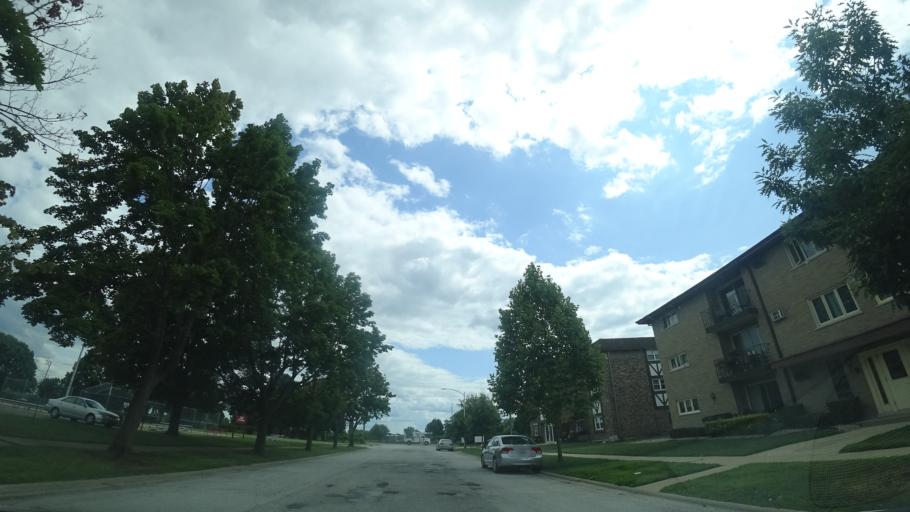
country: US
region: Illinois
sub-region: Cook County
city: Alsip
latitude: 41.6921
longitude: -87.7373
